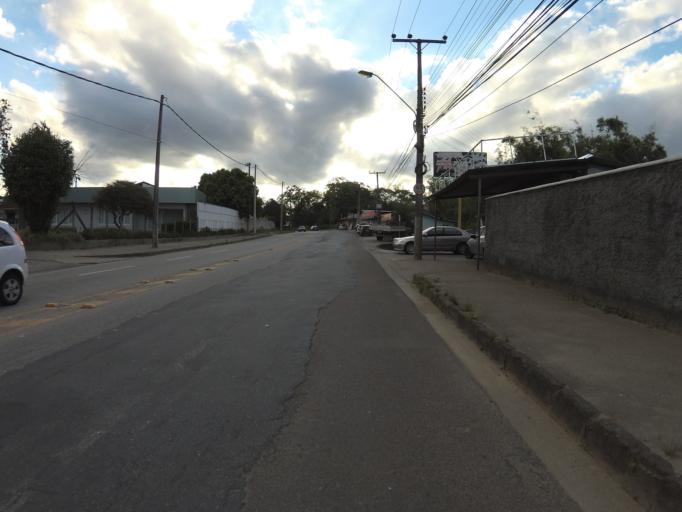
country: BR
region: Santa Catarina
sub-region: Blumenau
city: Blumenau
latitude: -26.8867
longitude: -49.1171
